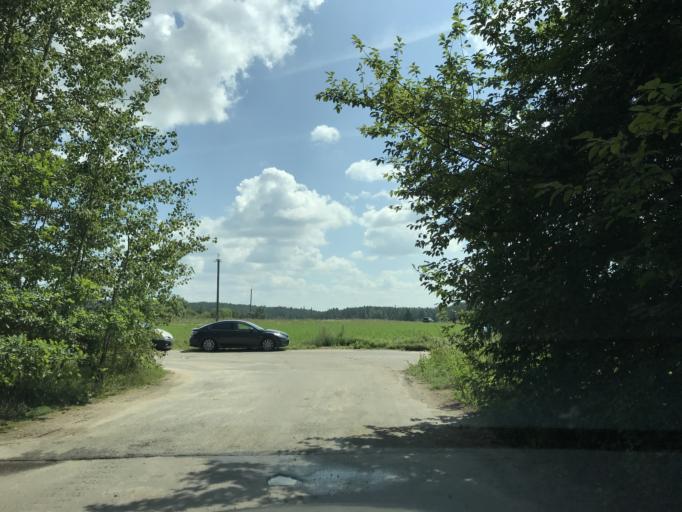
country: BY
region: Minsk
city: Rakaw
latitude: 54.0096
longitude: 26.9801
